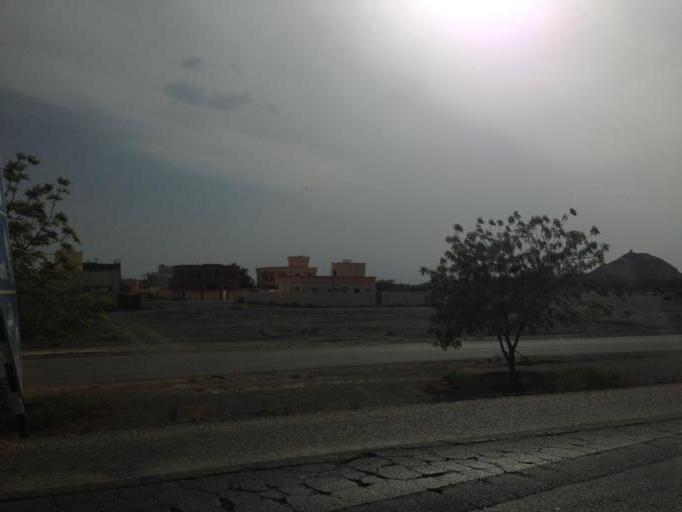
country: OM
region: Ash Sharqiyah
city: Al Qabil
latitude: 22.5765
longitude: 58.6928
